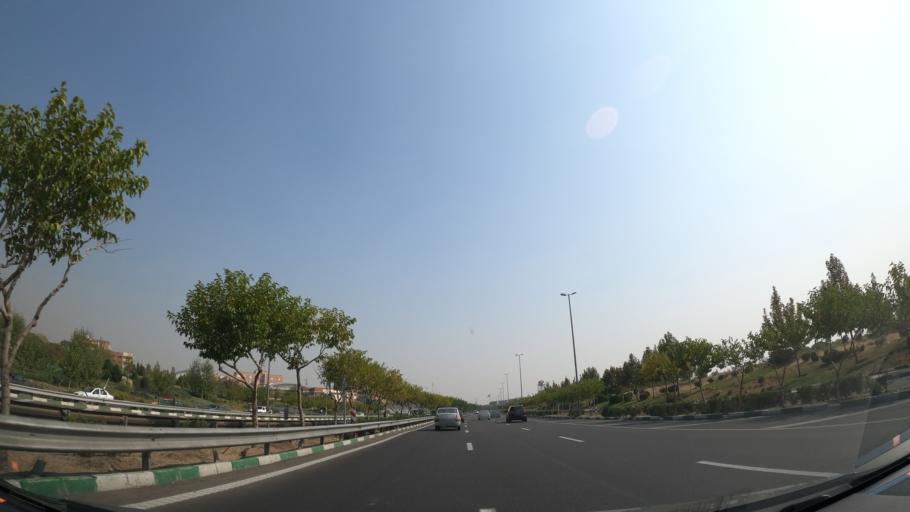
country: IR
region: Tehran
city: Shahr-e Qods
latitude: 35.7595
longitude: 51.2563
